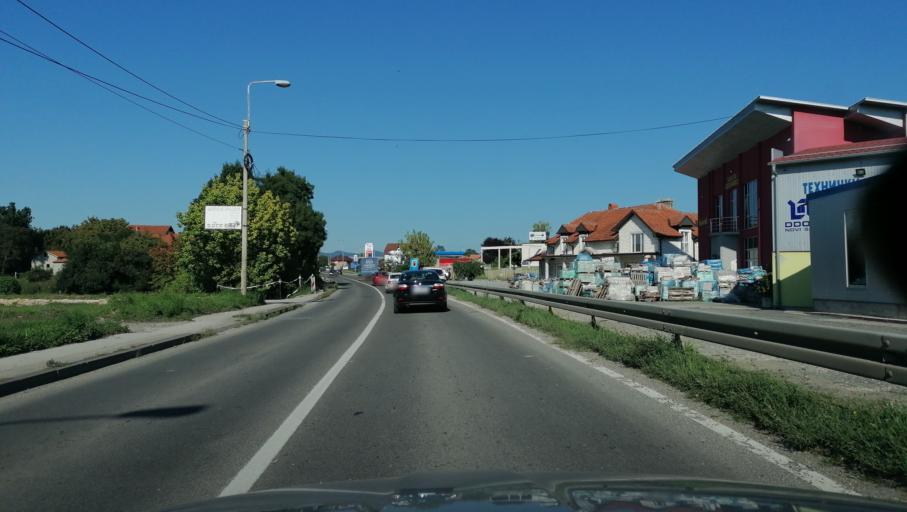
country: RS
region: Central Serbia
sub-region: Raski Okrug
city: Kraljevo
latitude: 43.7212
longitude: 20.6425
